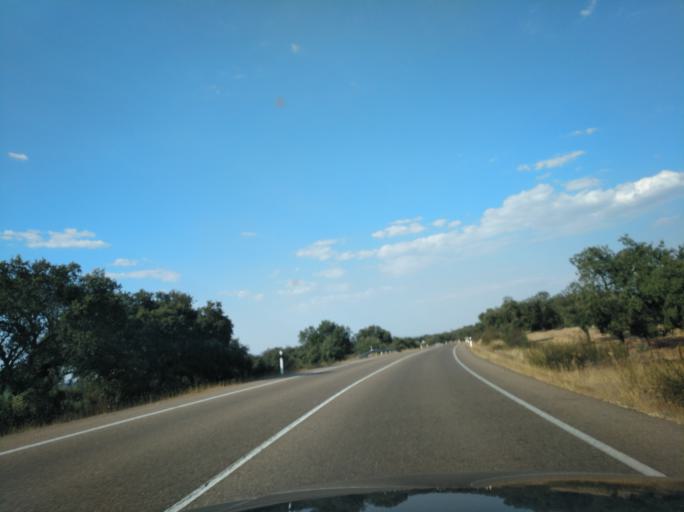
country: ES
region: Extremadura
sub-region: Provincia de Badajoz
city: Villanueva del Fresno
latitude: 38.4115
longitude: -7.1385
